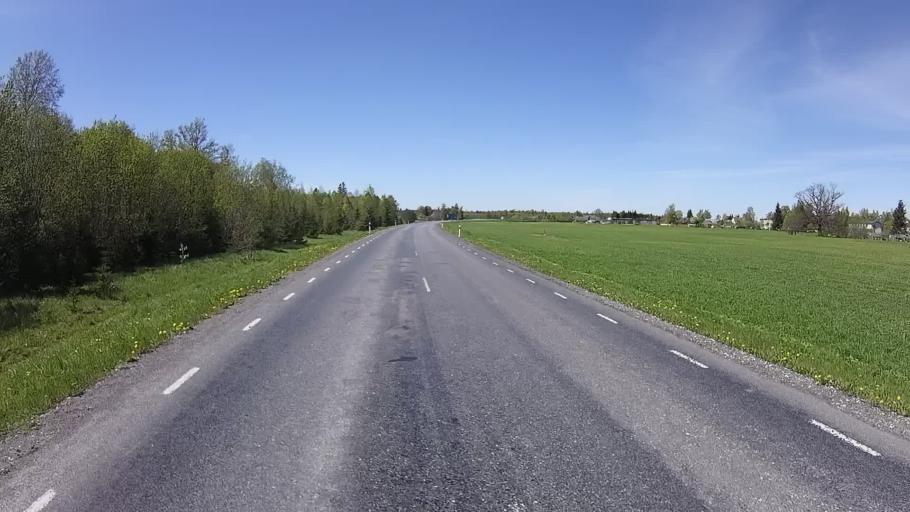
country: EE
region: Raplamaa
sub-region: Kehtna vald
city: Kehtna
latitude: 59.0543
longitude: 24.9597
